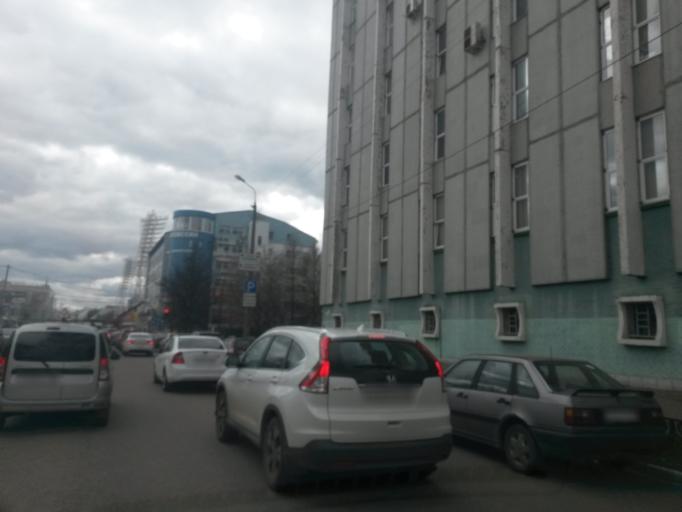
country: RU
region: Jaroslavl
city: Yaroslavl
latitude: 57.6315
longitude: 39.8697
